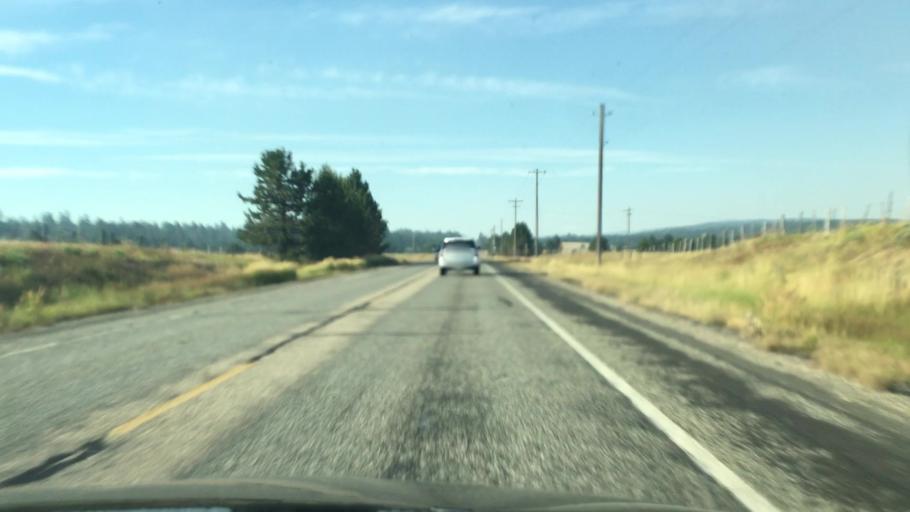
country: US
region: Idaho
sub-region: Valley County
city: Cascade
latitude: 44.3505
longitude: -116.0252
